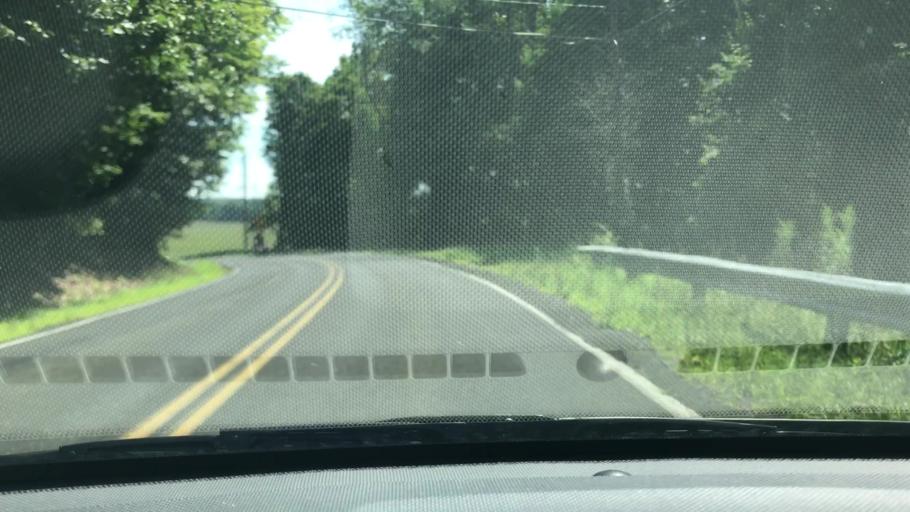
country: US
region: New York
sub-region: Ulster County
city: Stone Ridge
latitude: 41.8789
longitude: -74.1401
